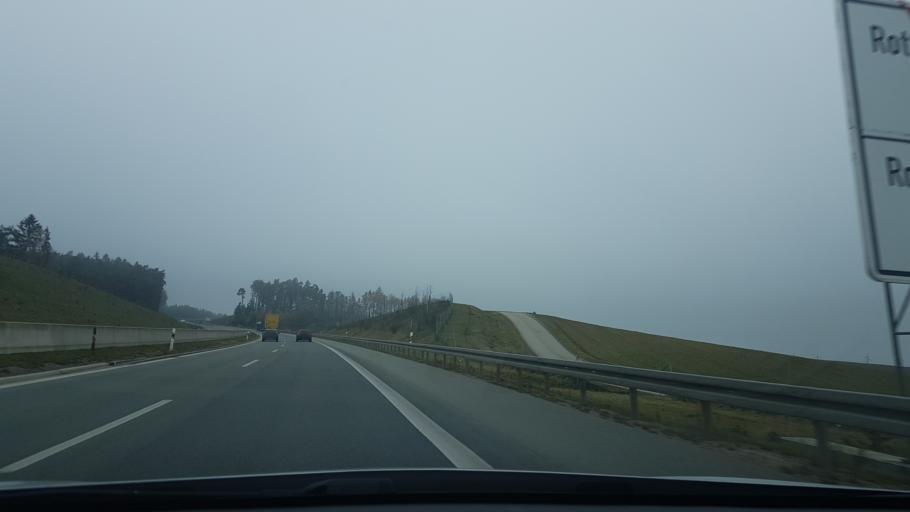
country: DE
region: Bavaria
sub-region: Lower Bavaria
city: Ergoldsbach
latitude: 48.7065
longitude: 12.1769
